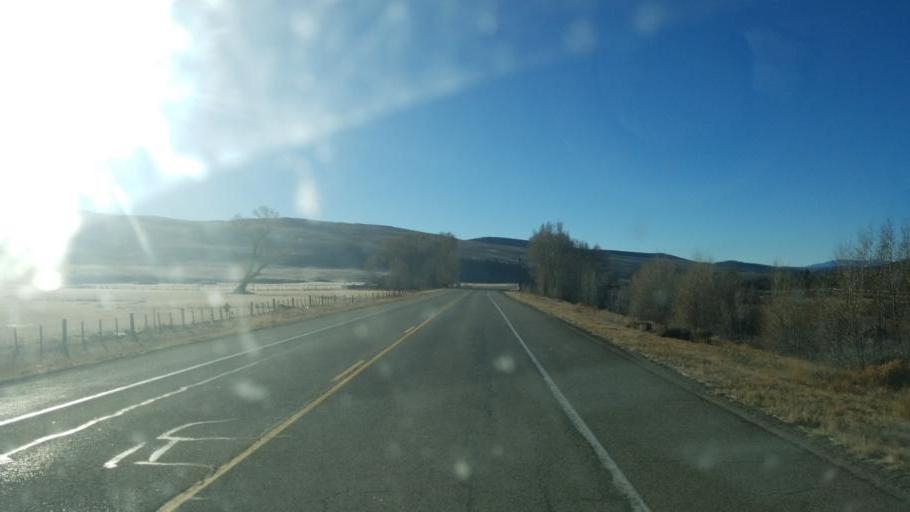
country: US
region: Colorado
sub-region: Gunnison County
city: Crested Butte
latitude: 38.7343
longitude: -106.8533
